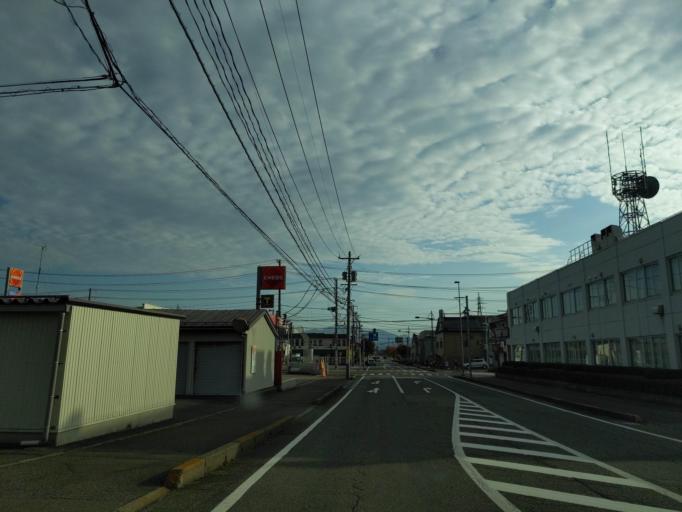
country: JP
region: Niigata
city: Kashiwazaki
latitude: 37.3692
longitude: 138.5604
